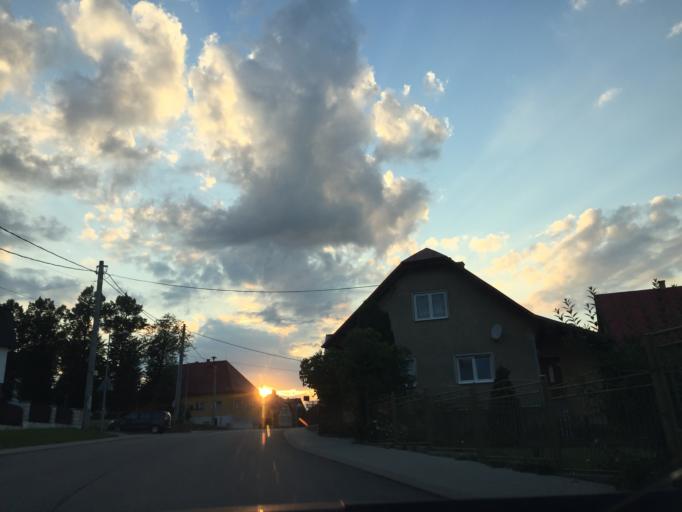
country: PL
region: Silesian Voivodeship
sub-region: Powiat zywiecki
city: Korbielow
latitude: 49.4603
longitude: 19.3243
